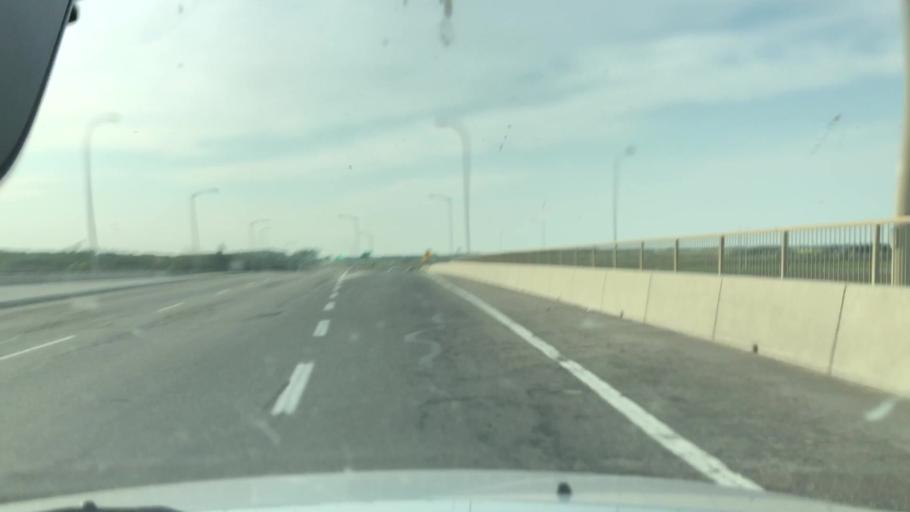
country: CA
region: Alberta
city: St. Albert
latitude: 53.6387
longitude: -113.5449
